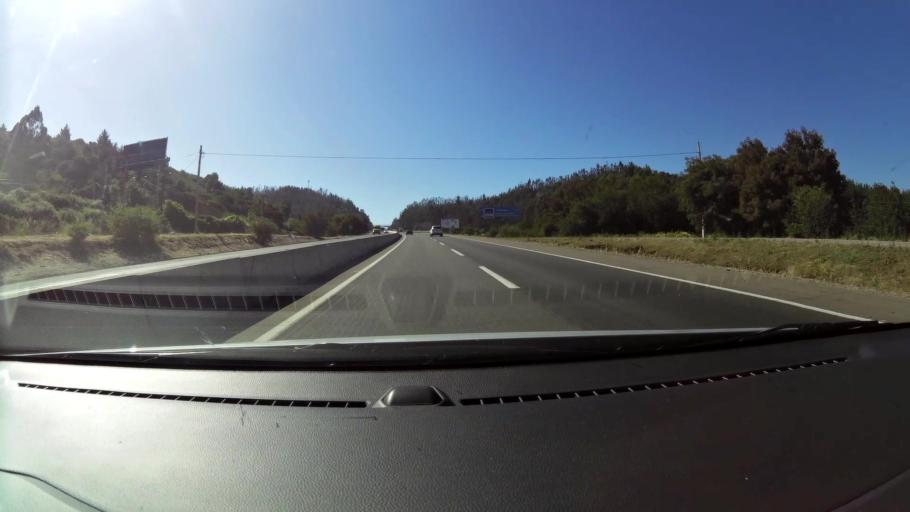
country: CL
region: Valparaiso
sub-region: Provincia de Marga Marga
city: Quilpue
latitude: -33.2135
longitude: -71.4755
